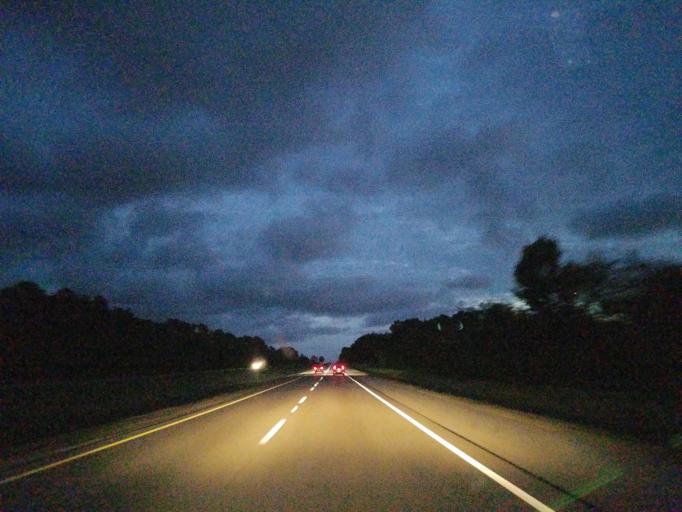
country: US
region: Mississippi
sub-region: Jones County
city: Sharon
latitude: 31.8311
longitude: -89.0507
